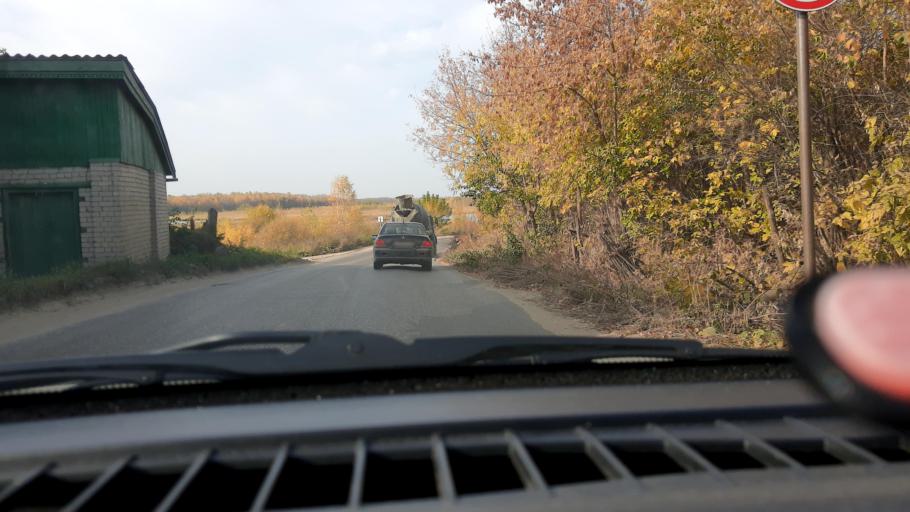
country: RU
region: Nizjnij Novgorod
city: Neklyudovo
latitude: 56.4120
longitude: 43.9754
